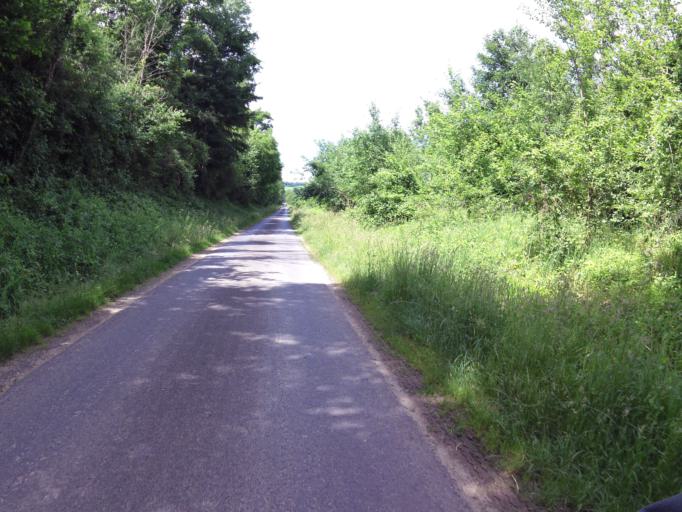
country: FR
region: Champagne-Ardenne
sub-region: Departement des Ardennes
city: Mouzon
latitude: 49.5372
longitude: 5.0872
